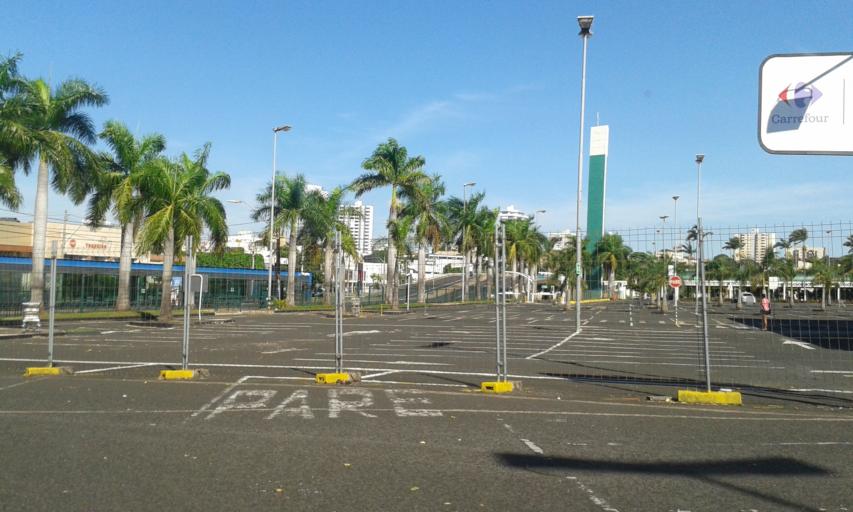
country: BR
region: Minas Gerais
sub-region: Uberlandia
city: Uberlandia
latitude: -18.9116
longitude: -48.2594
